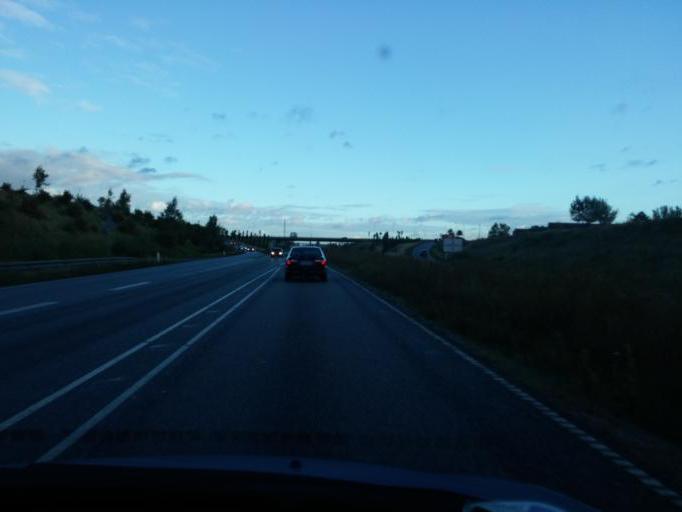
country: DK
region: South Denmark
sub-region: Odense Kommune
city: Neder Holluf
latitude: 55.3863
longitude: 10.4793
